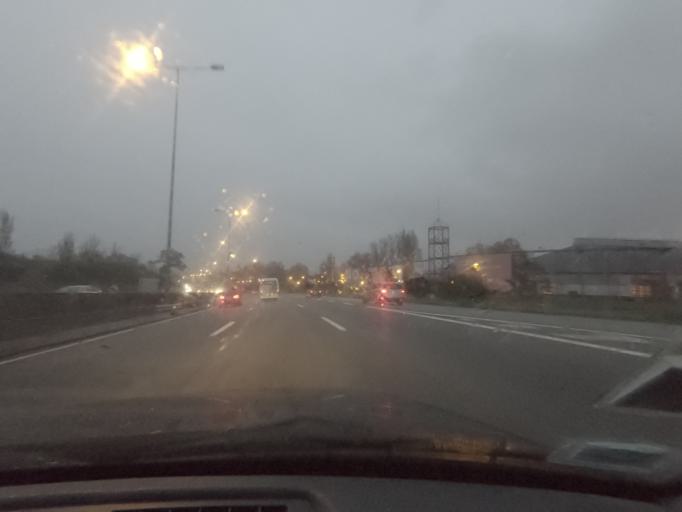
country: PT
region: Porto
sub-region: Matosinhos
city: Leca da Palmeira
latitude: 41.2023
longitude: -8.6899
